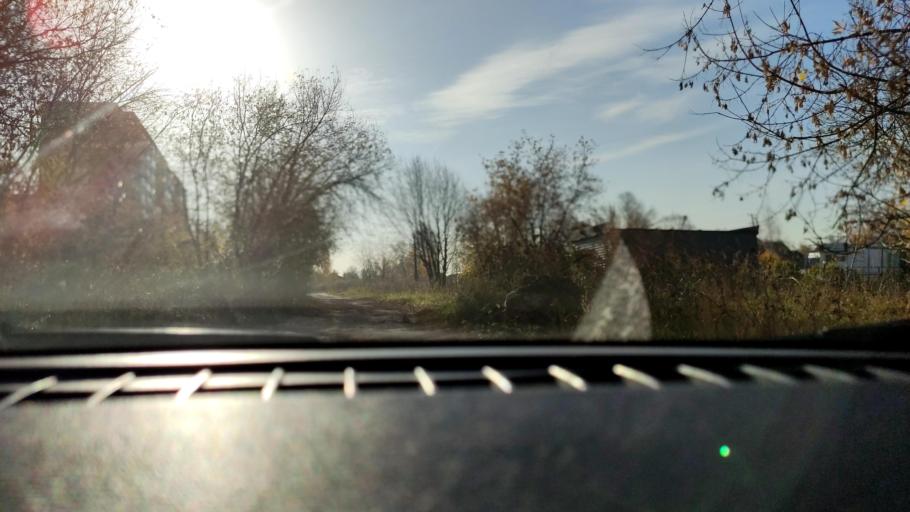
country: RU
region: Perm
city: Perm
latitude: 58.0308
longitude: 56.3197
